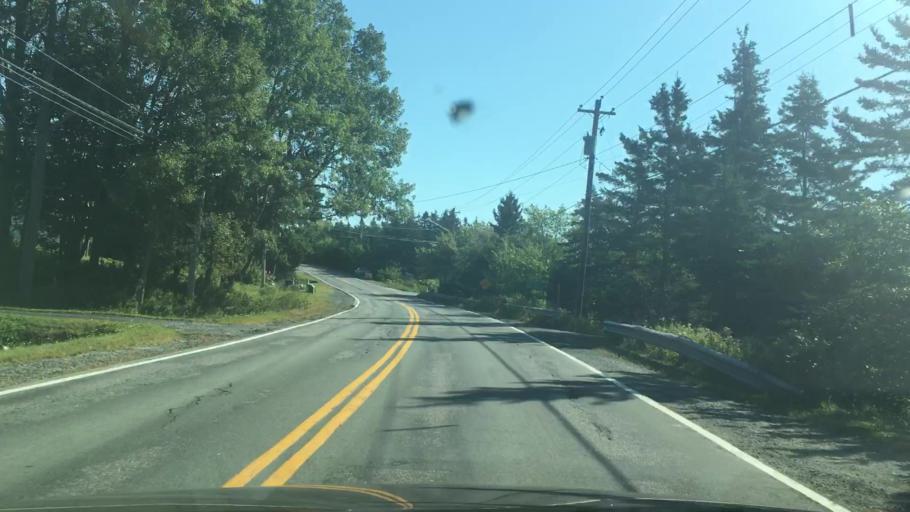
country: CA
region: Nova Scotia
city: Cole Harbour
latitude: 44.7765
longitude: -63.0686
